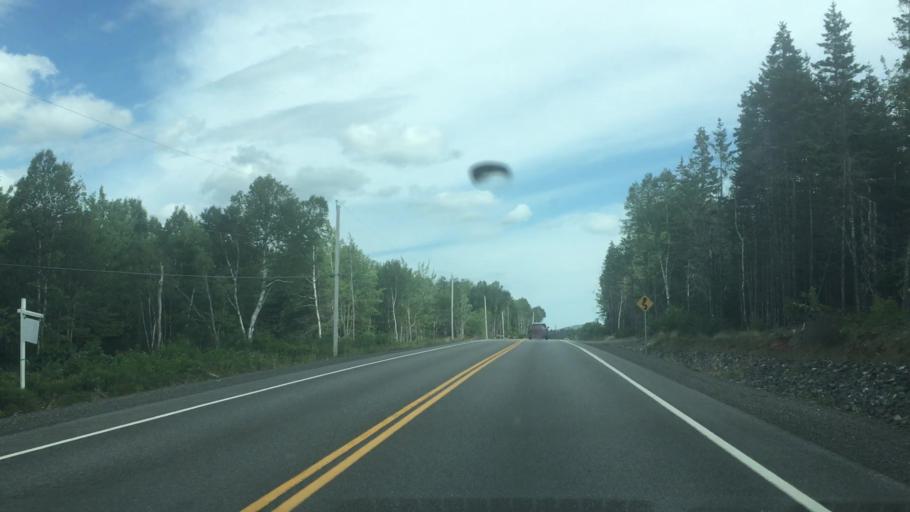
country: CA
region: Nova Scotia
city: Sydney Mines
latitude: 46.3130
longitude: -60.6135
